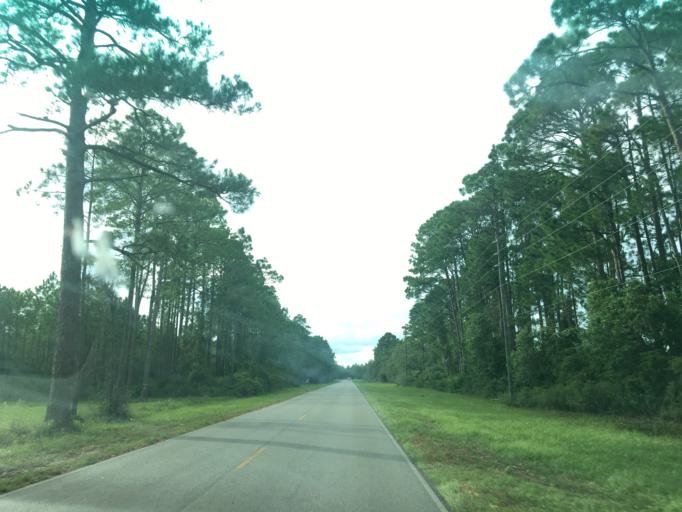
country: US
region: Florida
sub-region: Wakulla County
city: Crawfordville
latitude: 29.9398
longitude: -84.3831
